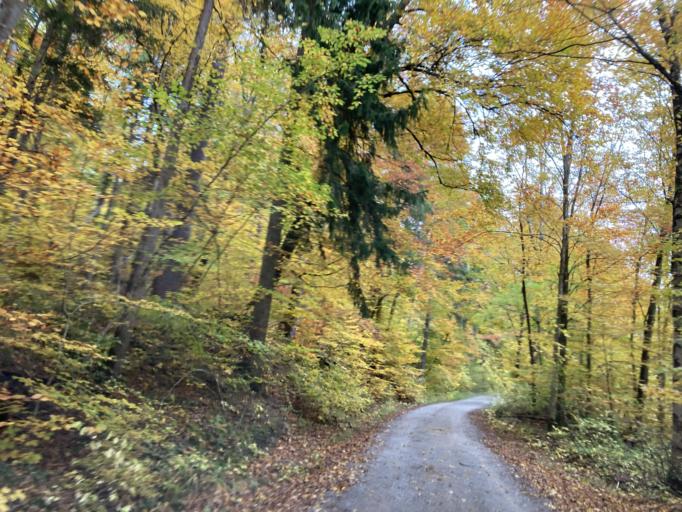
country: DE
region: Baden-Wuerttemberg
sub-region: Tuebingen Region
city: Dusslingen
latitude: 48.4674
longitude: 8.9996
